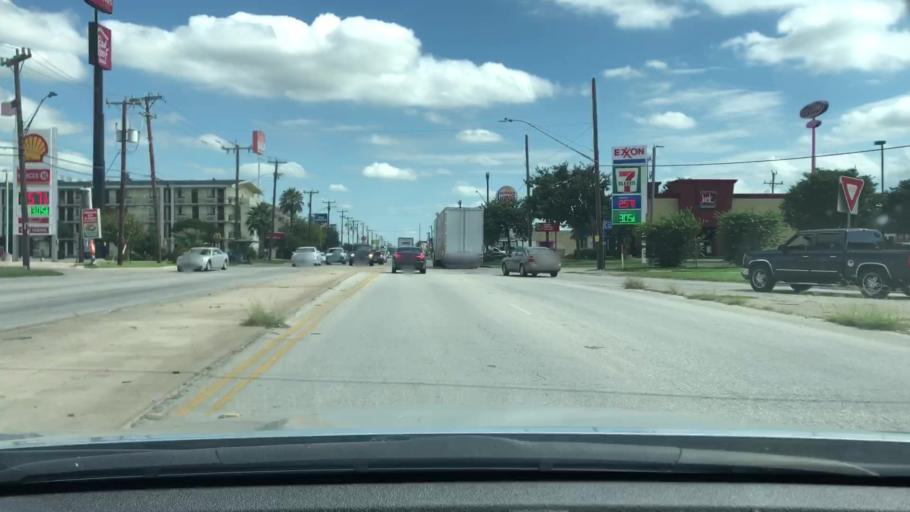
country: US
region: Texas
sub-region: Bexar County
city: Kirby
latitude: 29.4841
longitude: -98.4026
